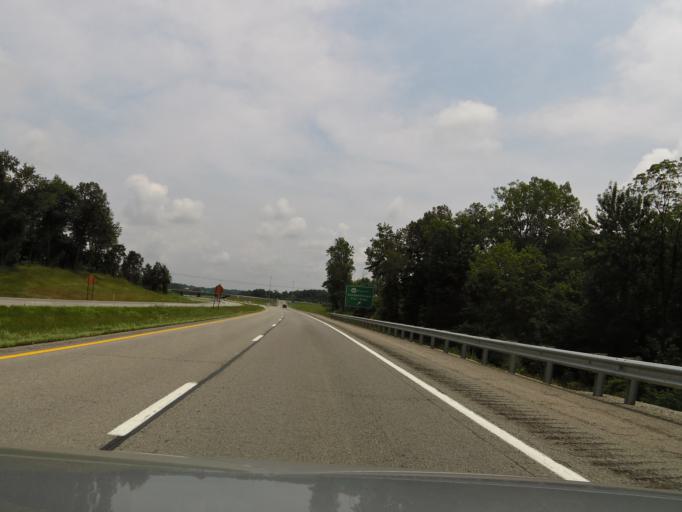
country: US
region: Kentucky
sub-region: Hardin County
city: Elizabethtown
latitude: 37.6505
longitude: -85.8955
